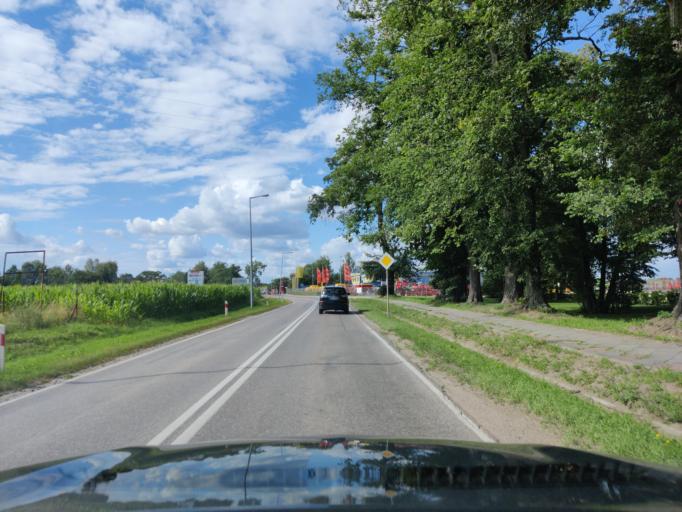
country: PL
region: Podlasie
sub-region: Powiat wysokomazowiecki
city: Czyzew
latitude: 52.8017
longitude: 22.3103
